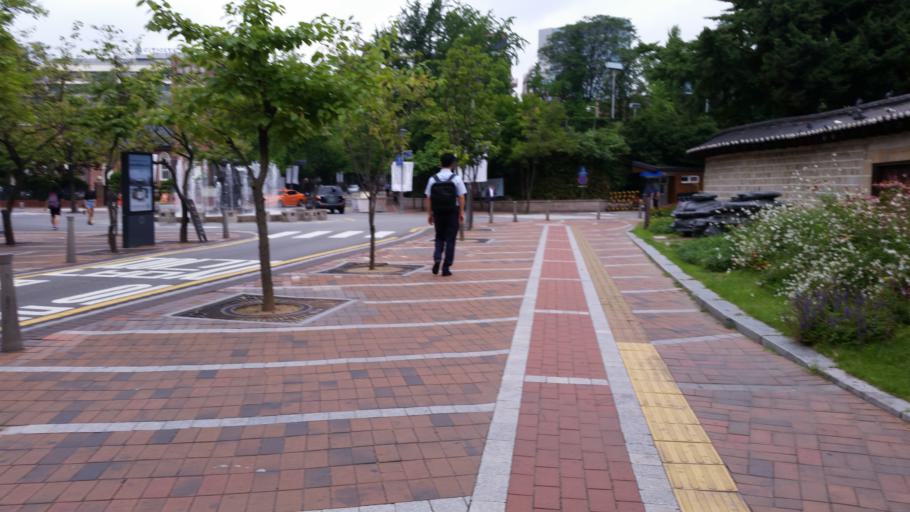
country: KR
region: Seoul
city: Seoul
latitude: 37.5651
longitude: 126.9738
